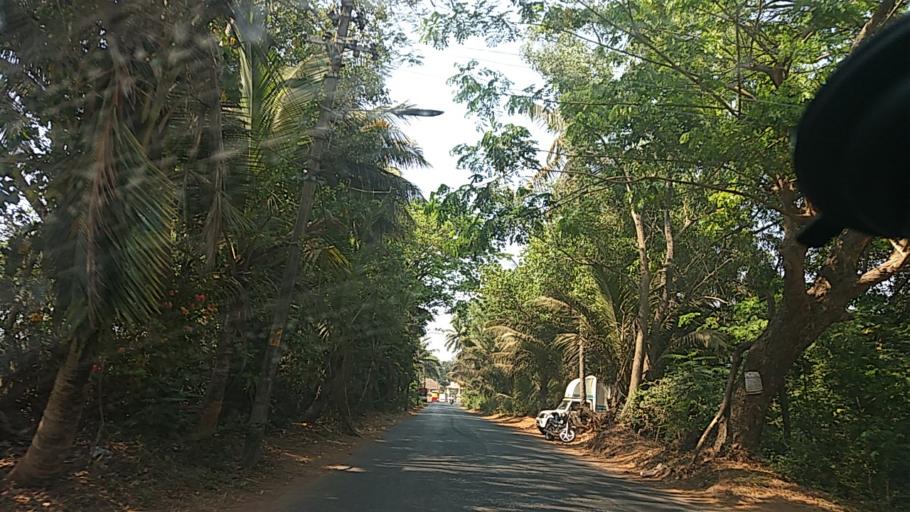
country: IN
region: Goa
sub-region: North Goa
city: Saligao
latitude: 15.5439
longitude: 73.7893
